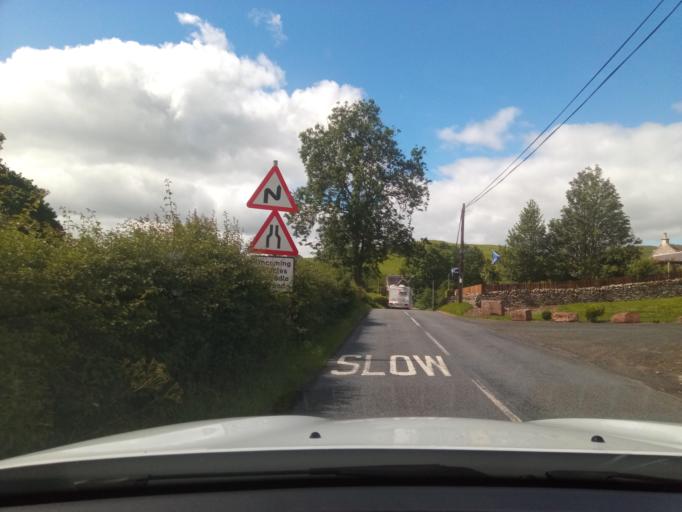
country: GB
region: Scotland
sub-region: The Scottish Borders
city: Innerleithen
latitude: 55.5554
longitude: -2.9692
